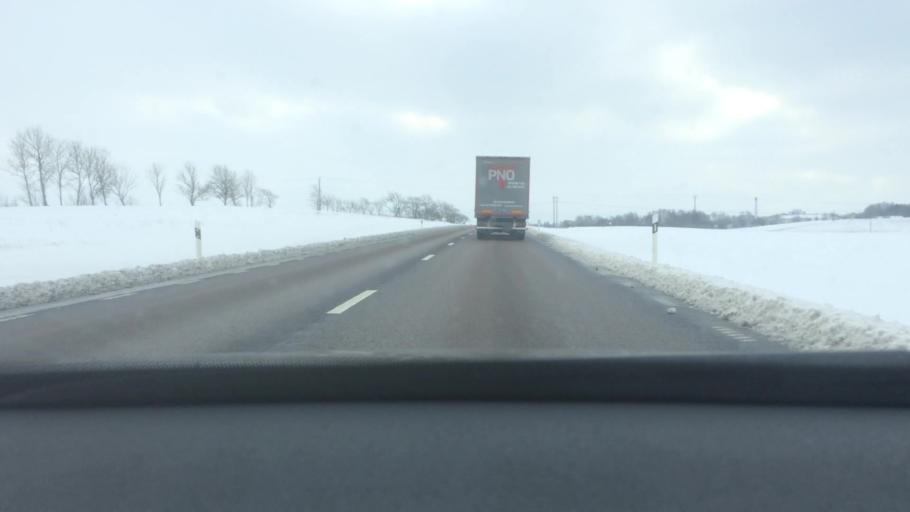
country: SE
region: Vaestra Goetaland
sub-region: Falkopings Kommun
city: Falkoeping
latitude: 58.2012
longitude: 13.5614
